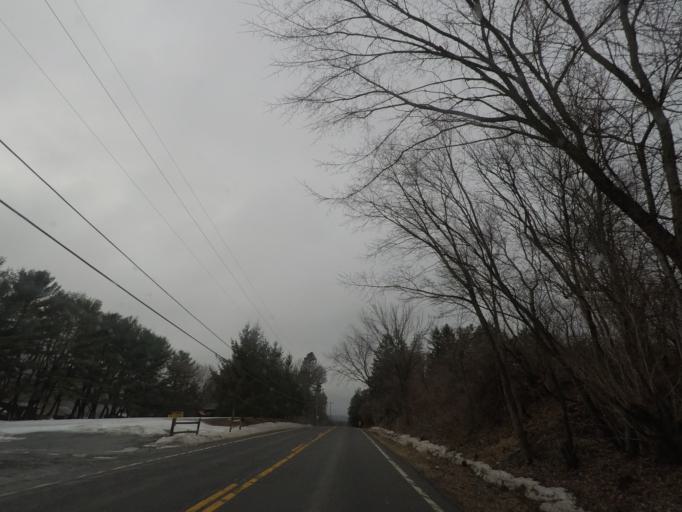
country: US
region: New York
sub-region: Albany County
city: Voorheesville
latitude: 42.6557
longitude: -73.9736
